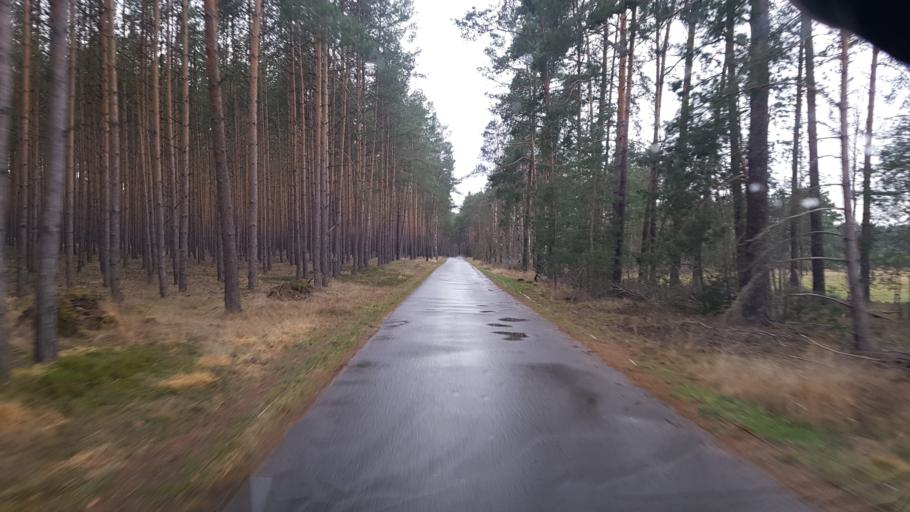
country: DE
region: Brandenburg
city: Crinitz
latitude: 51.6659
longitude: 13.8148
